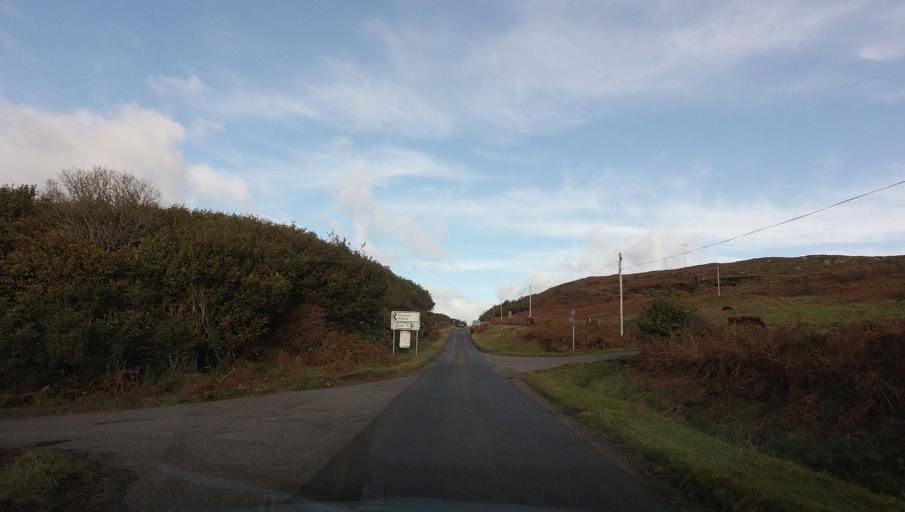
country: GB
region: Scotland
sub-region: Argyll and Bute
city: Isle Of Mull
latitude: 56.3282
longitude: -6.1996
